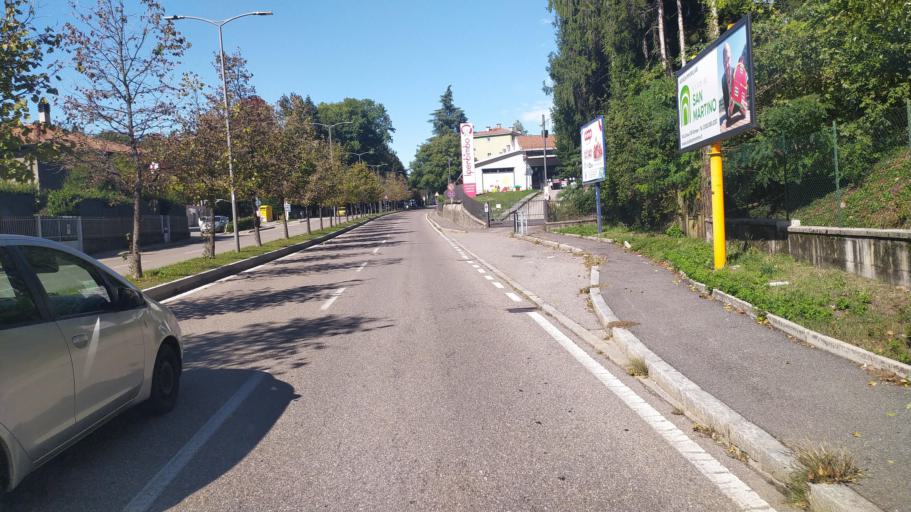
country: IT
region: Lombardy
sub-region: Provincia di Varese
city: Varese
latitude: 45.8041
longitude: 8.8329
